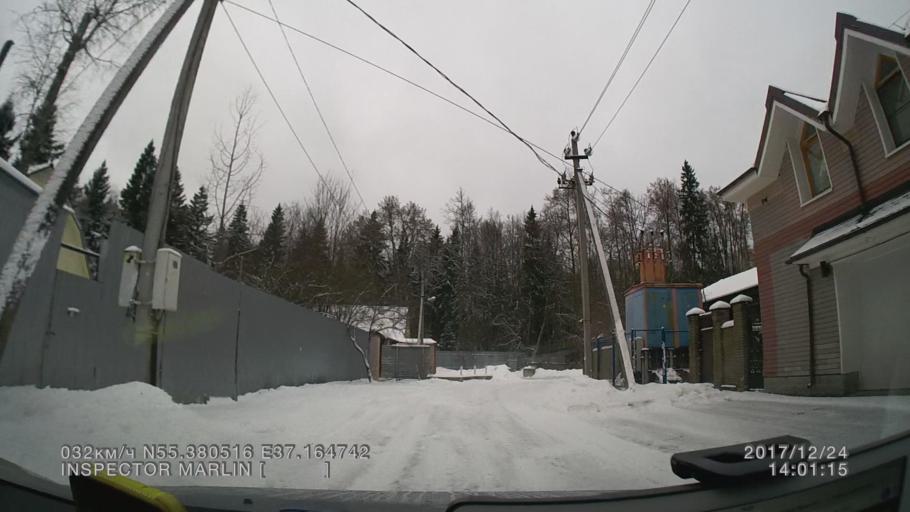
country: RU
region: Moskovskaya
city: Troitsk
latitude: 55.3806
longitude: 37.1646
